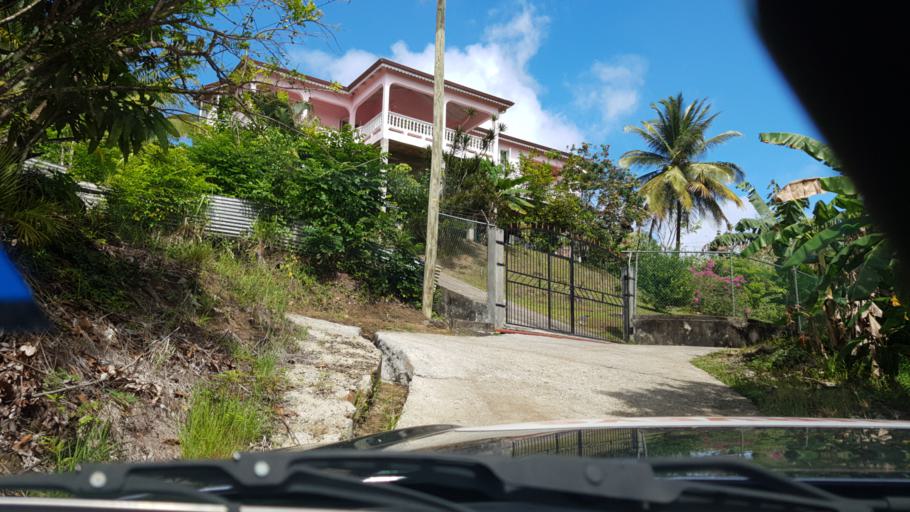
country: LC
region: Anse-la-Raye
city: Anse La Raye
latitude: 13.9469
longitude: -61.0359
